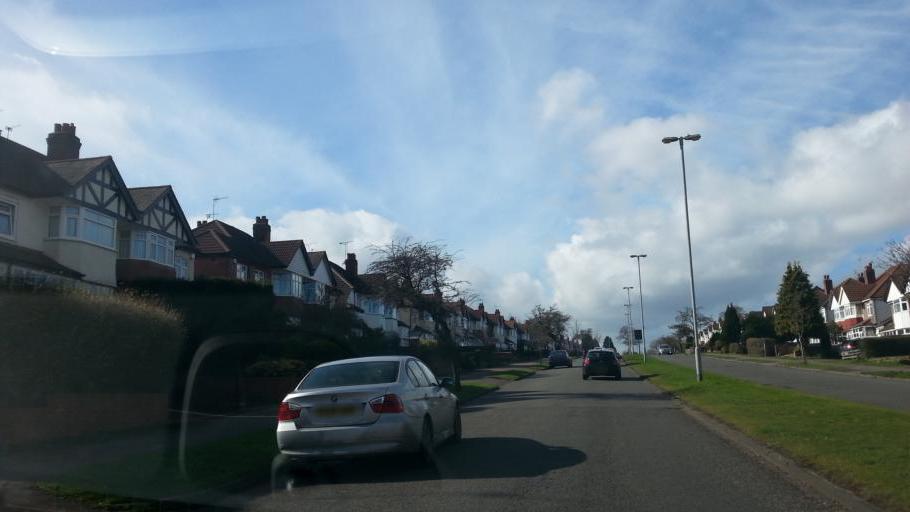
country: GB
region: England
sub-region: City and Borough of Birmingham
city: Bartley Green
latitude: 52.4479
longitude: -1.9592
